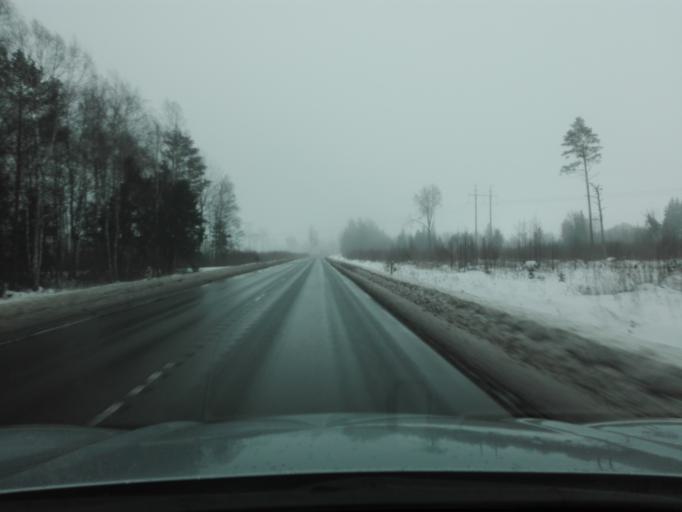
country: EE
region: Raplamaa
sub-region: Kohila vald
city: Kohila
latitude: 59.2357
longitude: 24.7663
